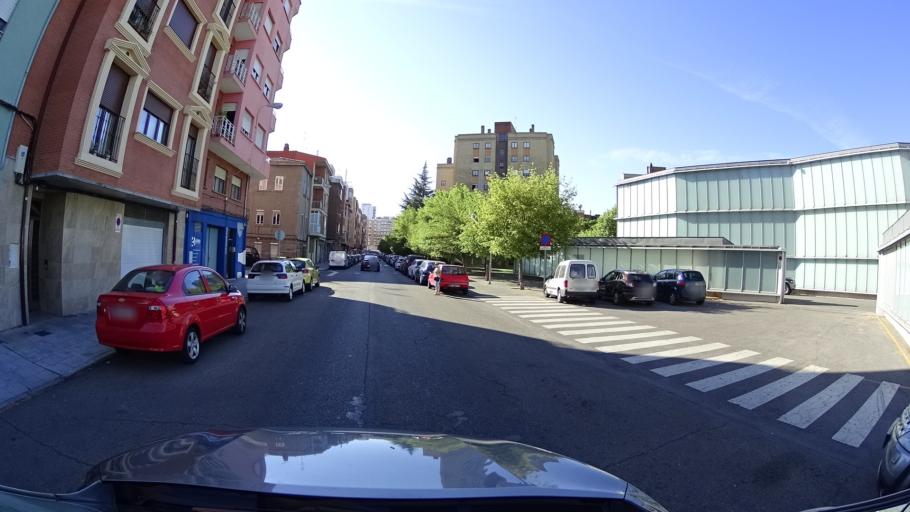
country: ES
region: Castille and Leon
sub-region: Provincia de Leon
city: Leon
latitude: 42.6070
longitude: -5.5816
